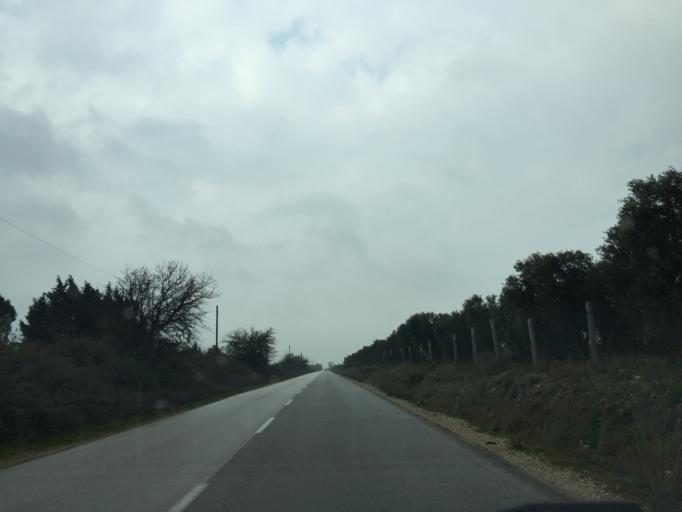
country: IT
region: Apulia
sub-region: Provincia di Foggia
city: Castelluccio dei Sauri
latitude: 41.4045
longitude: 15.4374
